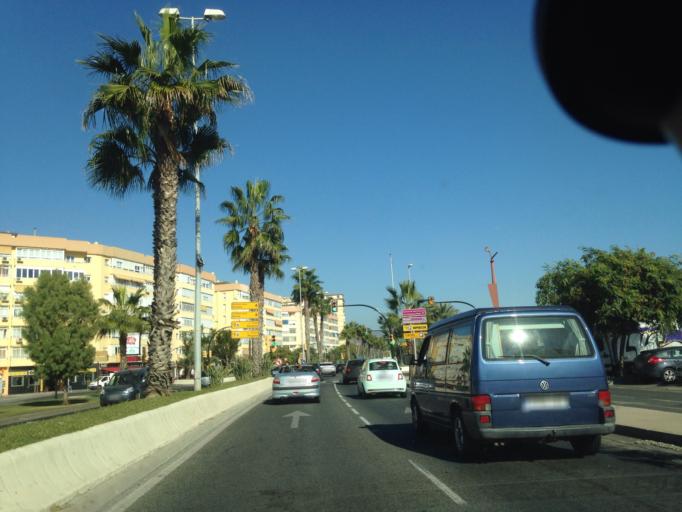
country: ES
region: Andalusia
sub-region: Provincia de Malaga
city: Malaga
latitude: 36.6996
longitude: -4.4366
